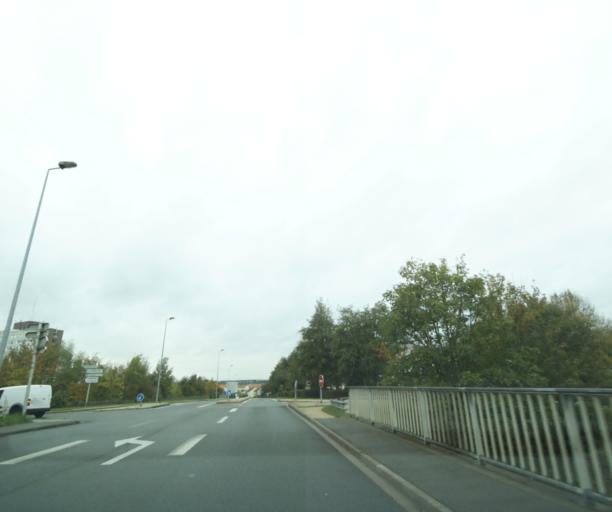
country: FR
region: Centre
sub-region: Departement d'Eure-et-Loir
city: Luray
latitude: 48.7280
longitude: 1.3890
